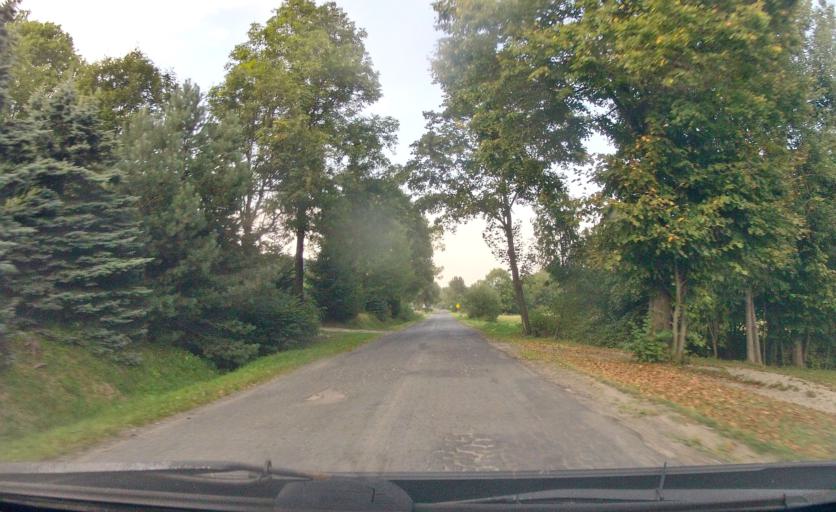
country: PL
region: Subcarpathian Voivodeship
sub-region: Powiat krosnienski
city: Dukla
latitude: 49.5382
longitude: 21.6161
